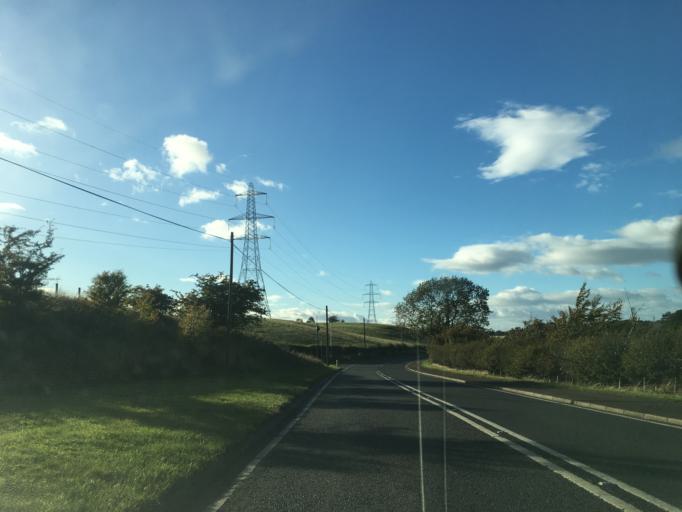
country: GB
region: Scotland
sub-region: Fife
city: Pathhead
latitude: 55.8454
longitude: -2.9276
